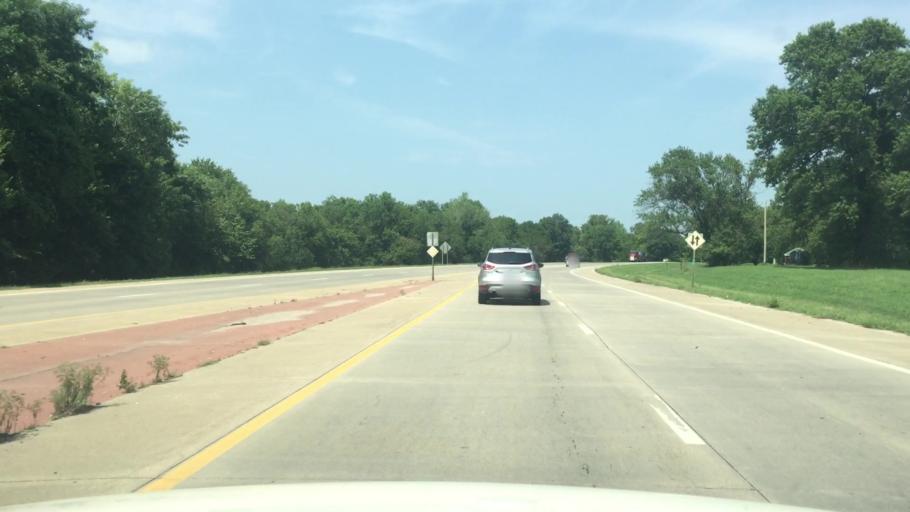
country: US
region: Kansas
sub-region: Crawford County
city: Pittsburg
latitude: 37.4138
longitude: -94.7227
